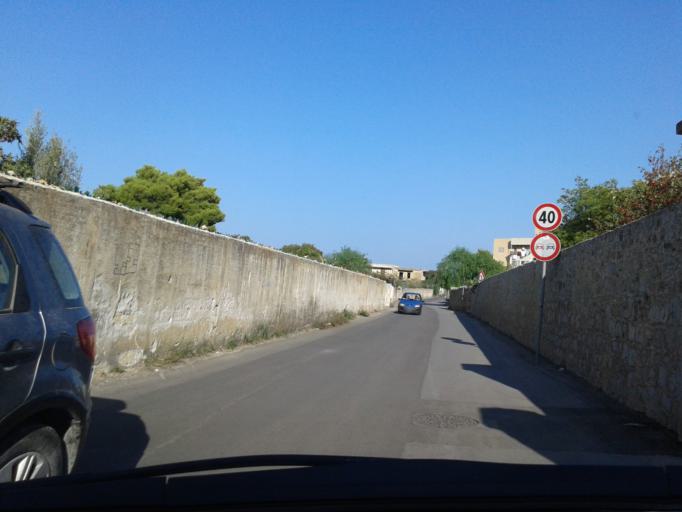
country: IT
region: Sicily
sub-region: Palermo
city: Monreale
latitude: 38.1031
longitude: 13.3157
